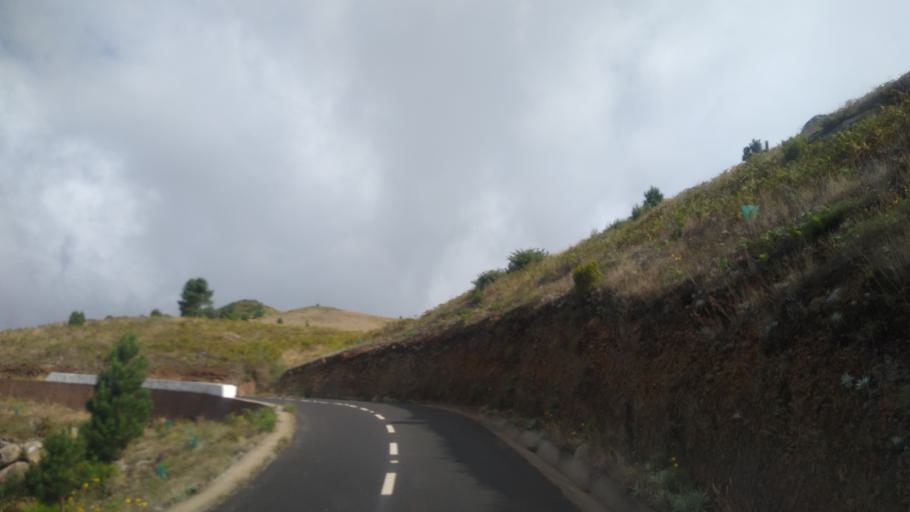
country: PT
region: Madeira
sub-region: Camara de Lobos
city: Curral das Freiras
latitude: 32.6987
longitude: -16.9394
